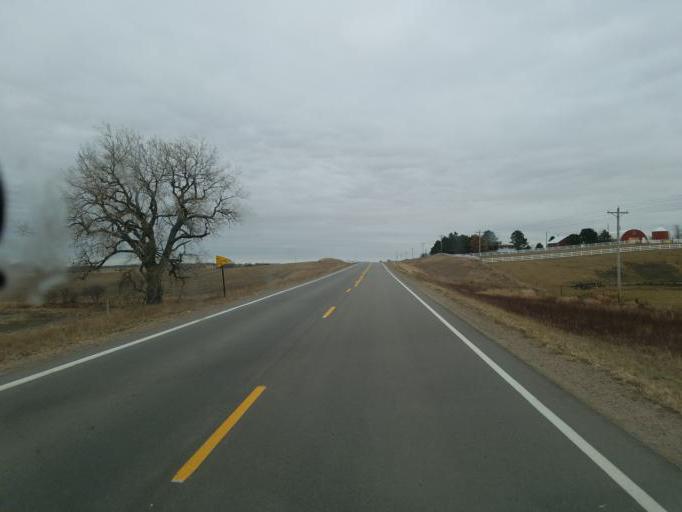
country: US
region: Nebraska
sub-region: Cedar County
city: Hartington
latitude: 42.6126
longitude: -97.3064
